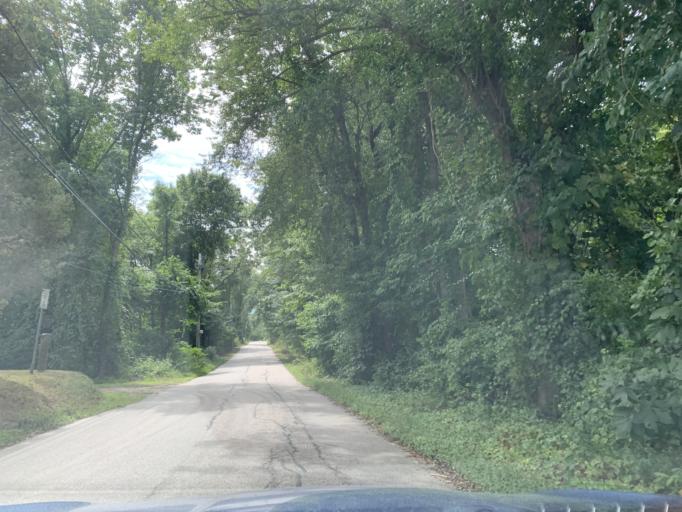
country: US
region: Rhode Island
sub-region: Kent County
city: West Greenwich
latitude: 41.5635
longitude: -71.6214
